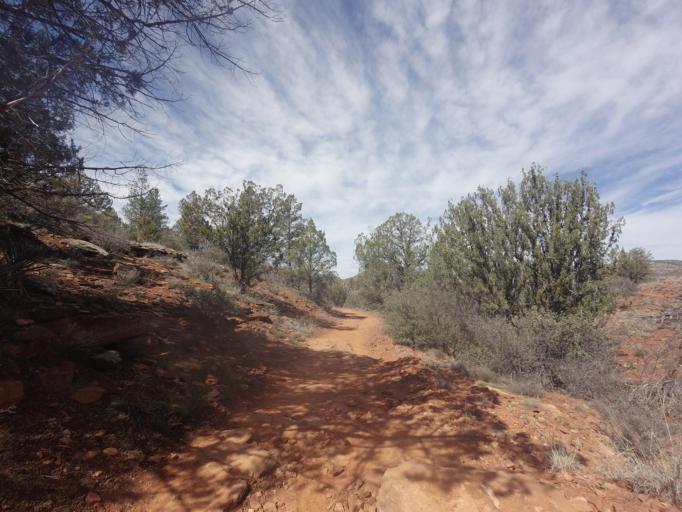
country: US
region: Arizona
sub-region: Yavapai County
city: West Sedona
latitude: 34.8093
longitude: -111.8222
